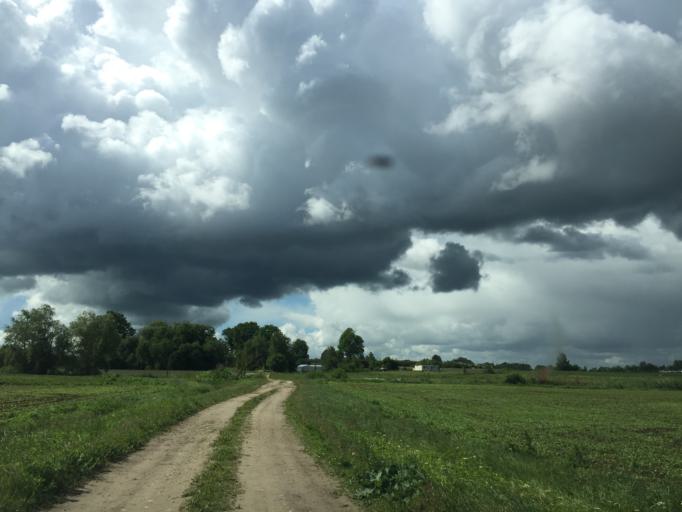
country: LV
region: Lecava
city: Iecava
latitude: 56.6103
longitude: 24.2032
